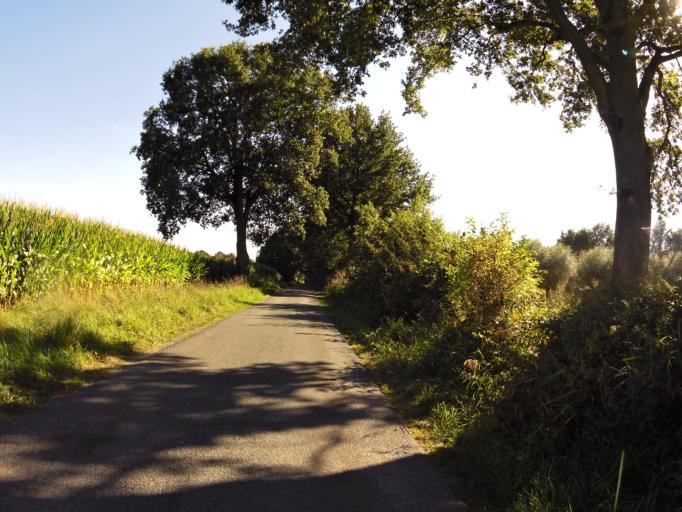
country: NL
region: Gelderland
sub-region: Gemeente Winterswijk
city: Winterswijk
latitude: 52.0422
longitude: 6.7177
